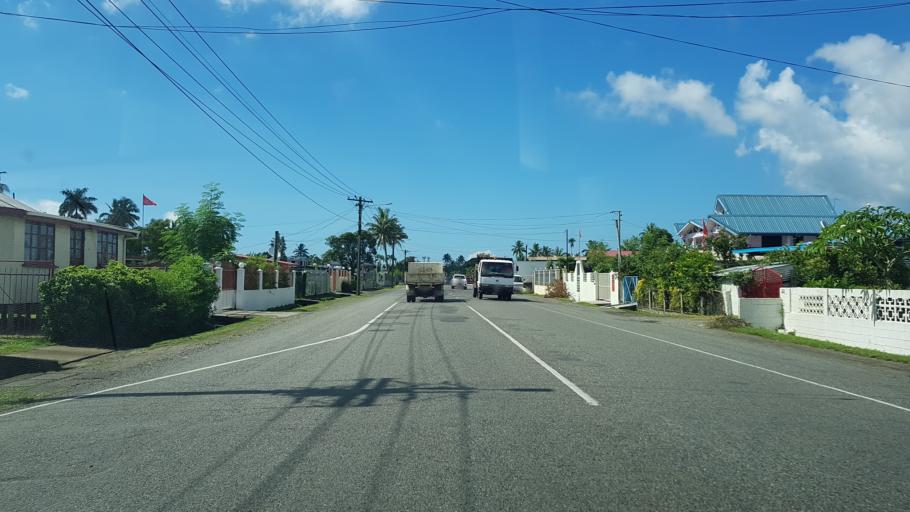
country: FJ
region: Central
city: Suva
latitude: -18.1298
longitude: 178.4593
